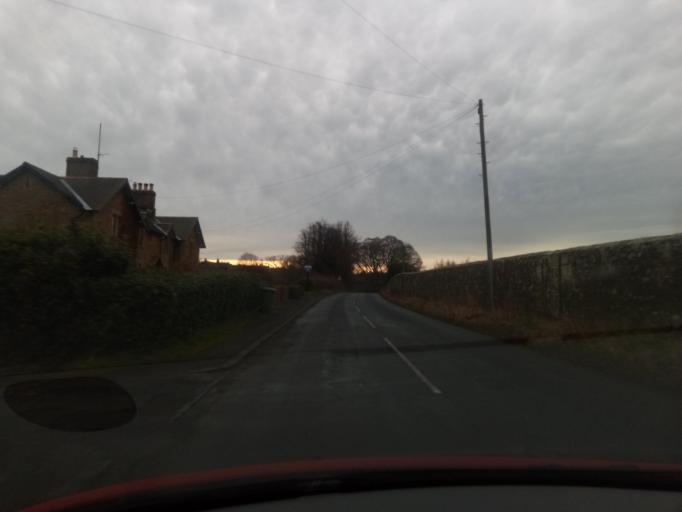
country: GB
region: England
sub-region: Northumberland
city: Alnwick
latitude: 55.4241
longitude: -1.7173
